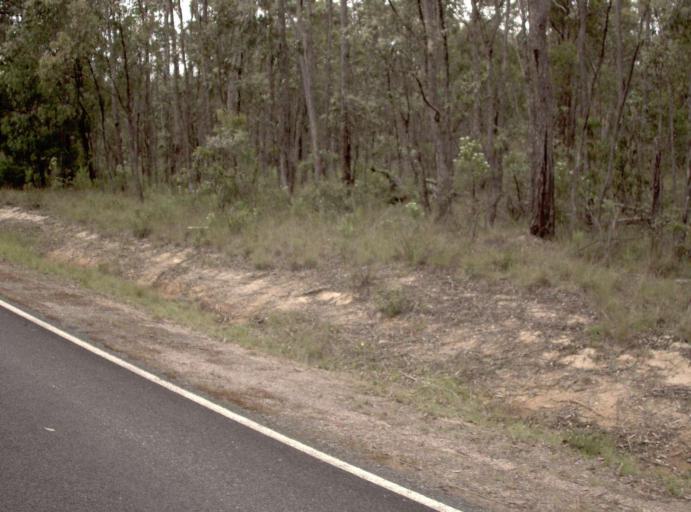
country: AU
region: Victoria
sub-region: East Gippsland
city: Bairnsdale
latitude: -37.6426
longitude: 147.2718
